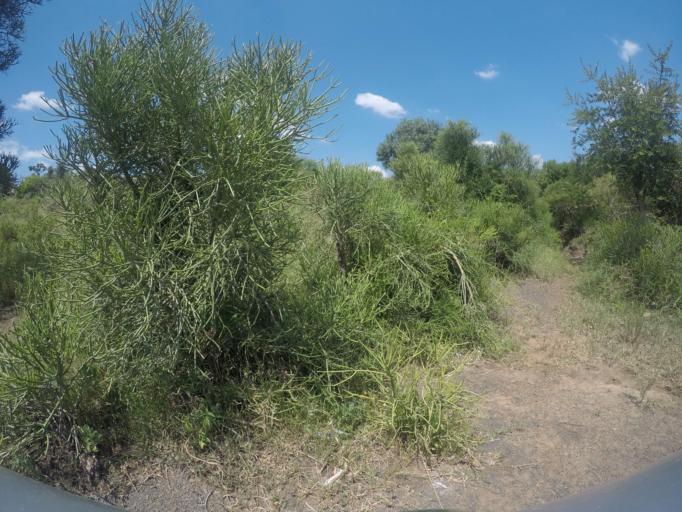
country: ZA
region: KwaZulu-Natal
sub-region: uThungulu District Municipality
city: Empangeni
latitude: -28.5988
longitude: 31.7360
